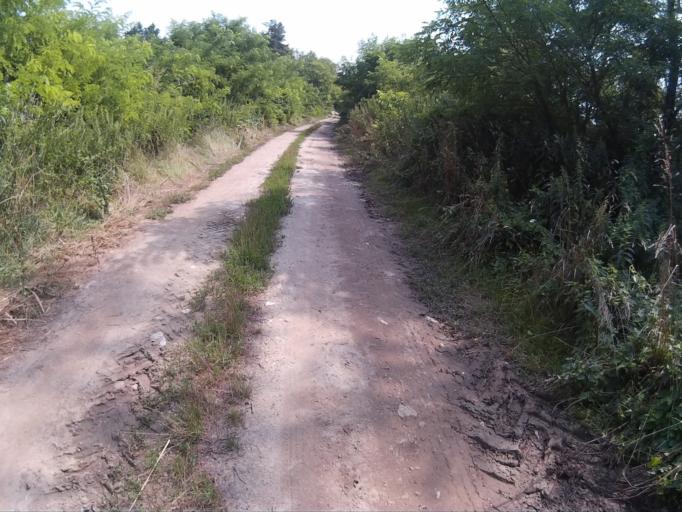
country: HU
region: Veszprem
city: Papa
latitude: 47.2893
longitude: 17.5800
